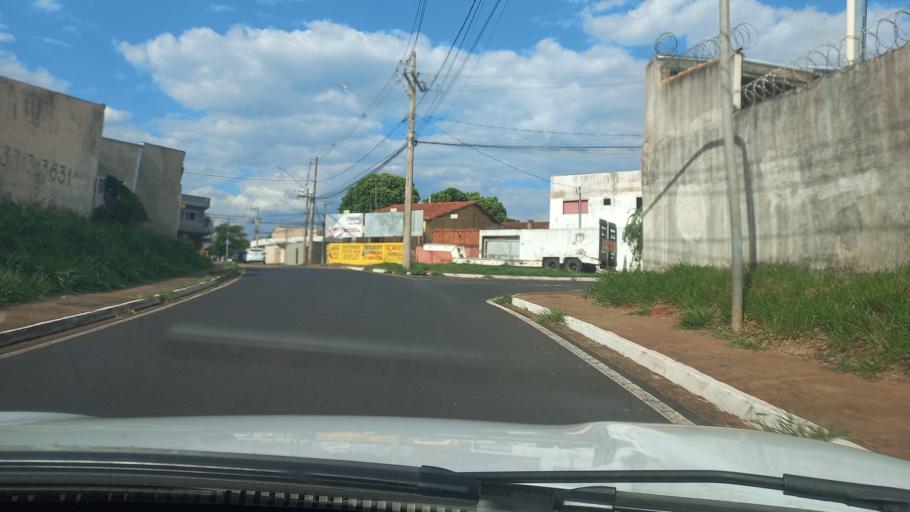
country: BR
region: Minas Gerais
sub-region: Uberaba
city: Uberaba
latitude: -19.7357
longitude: -47.9249
